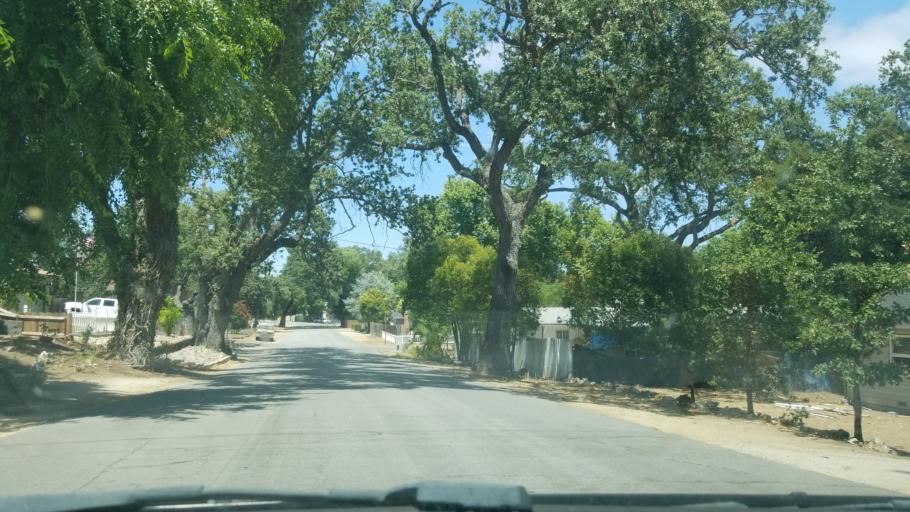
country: US
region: California
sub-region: San Luis Obispo County
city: Templeton
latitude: 35.5515
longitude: -120.7050
